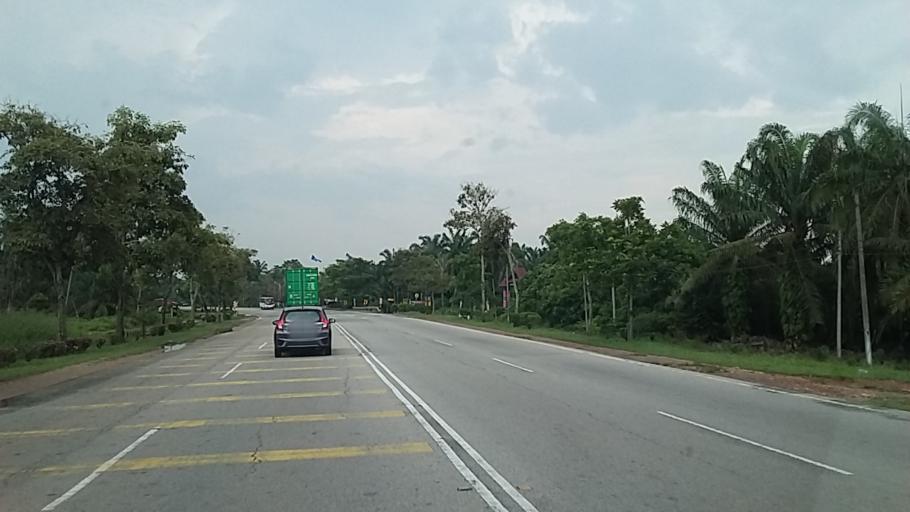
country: MY
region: Johor
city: Parit Raja
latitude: 1.8748
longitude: 103.1400
